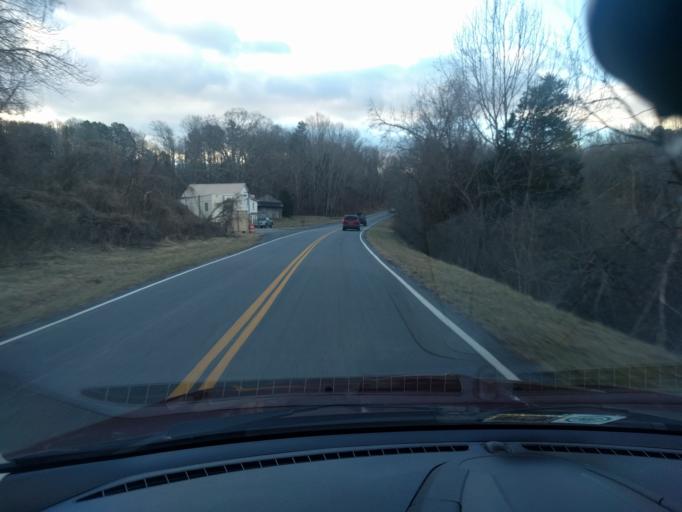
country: US
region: Virginia
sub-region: City of Bedford
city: Bedford
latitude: 37.3834
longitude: -79.5514
